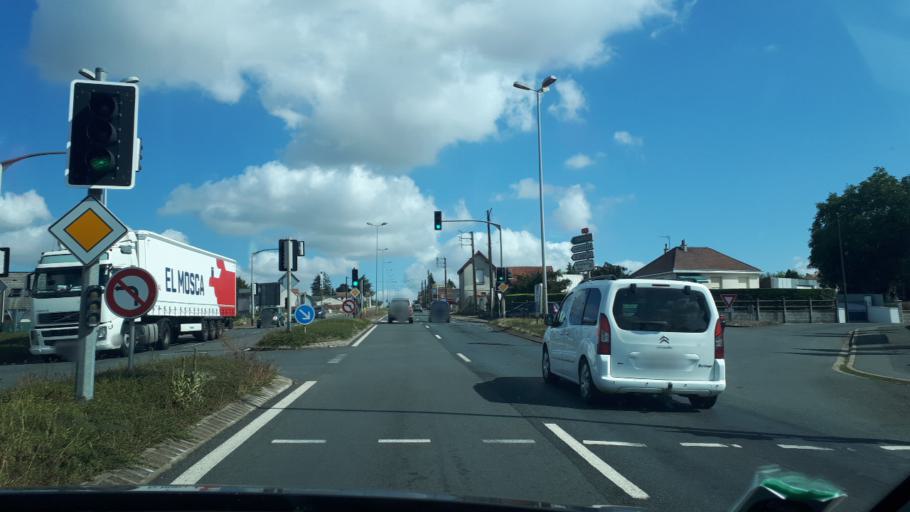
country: FR
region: Centre
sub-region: Departement du Loir-et-Cher
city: Saint-Ouen
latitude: 47.8105
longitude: 1.0737
